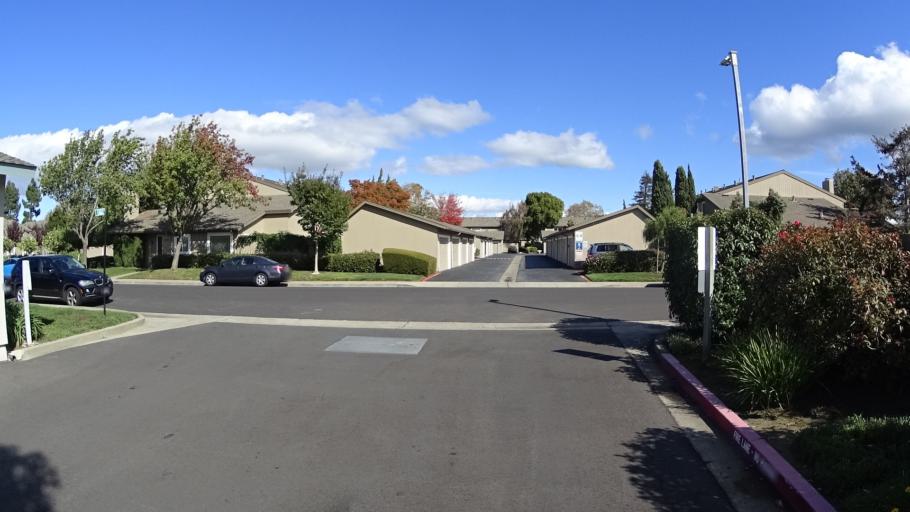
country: US
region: California
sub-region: San Mateo County
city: Foster City
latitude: 37.5633
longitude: -122.2534
